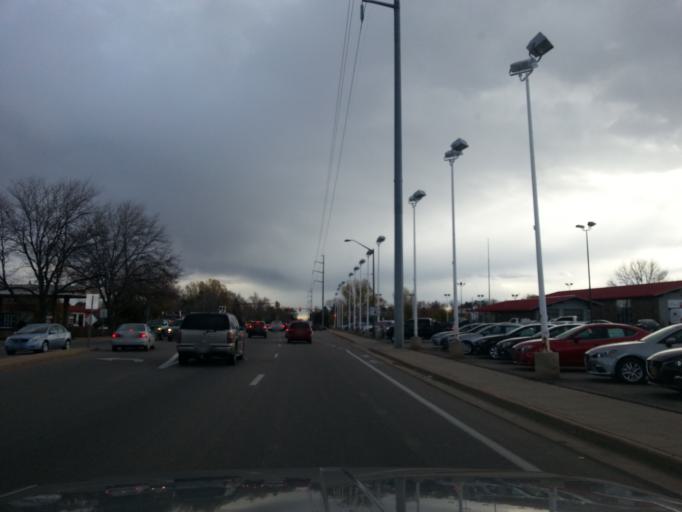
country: US
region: Colorado
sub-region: Larimer County
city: Fort Collins
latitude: 40.5525
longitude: -105.0792
